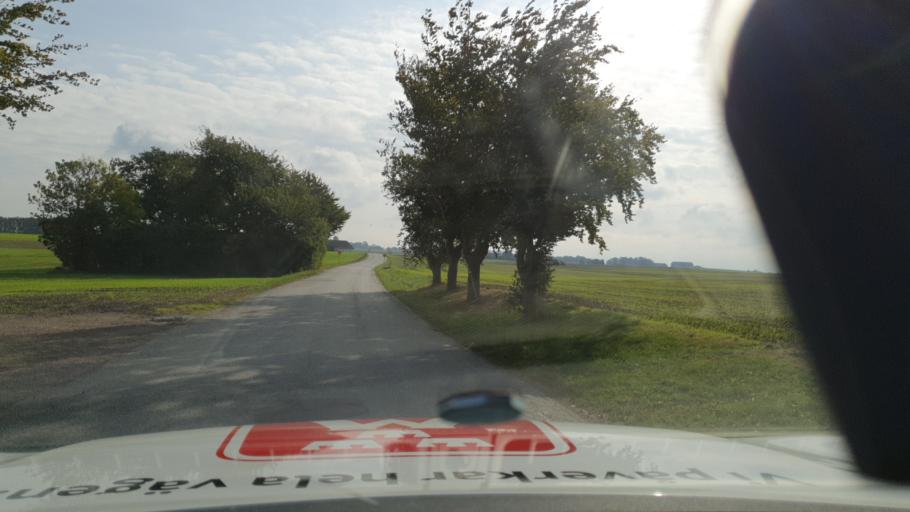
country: SE
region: Skane
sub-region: Trelleborgs Kommun
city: Trelleborg
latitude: 55.4235
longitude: 13.1104
